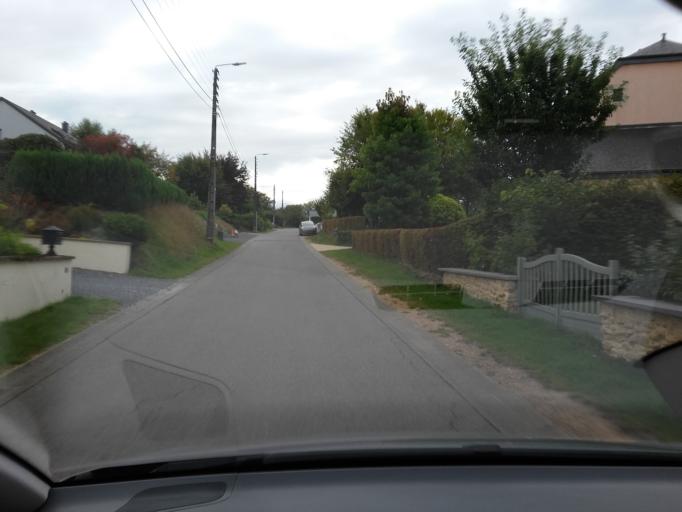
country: BE
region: Wallonia
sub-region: Province du Luxembourg
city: Saint-Leger
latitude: 49.6857
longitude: 5.6992
